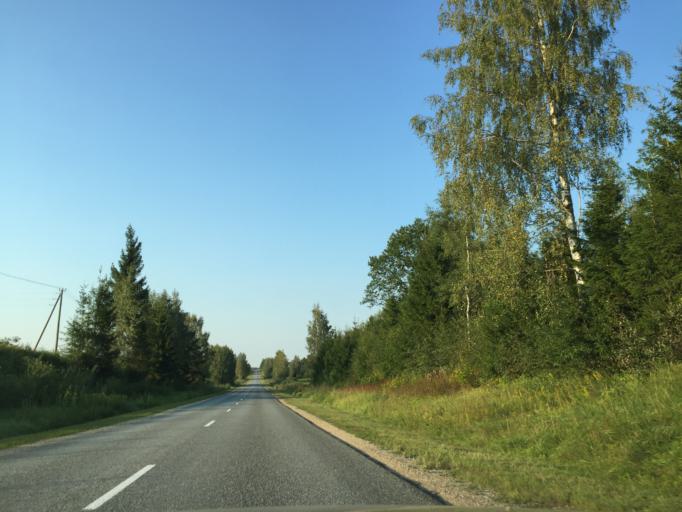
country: LV
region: Limbazu Rajons
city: Limbazi
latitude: 57.5620
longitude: 24.7659
